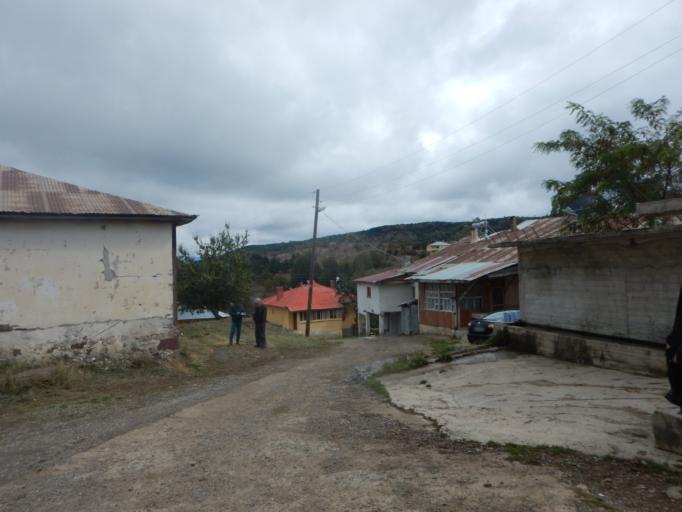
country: TR
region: Ordu
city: Mesudiye
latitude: 40.4342
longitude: 37.7794
